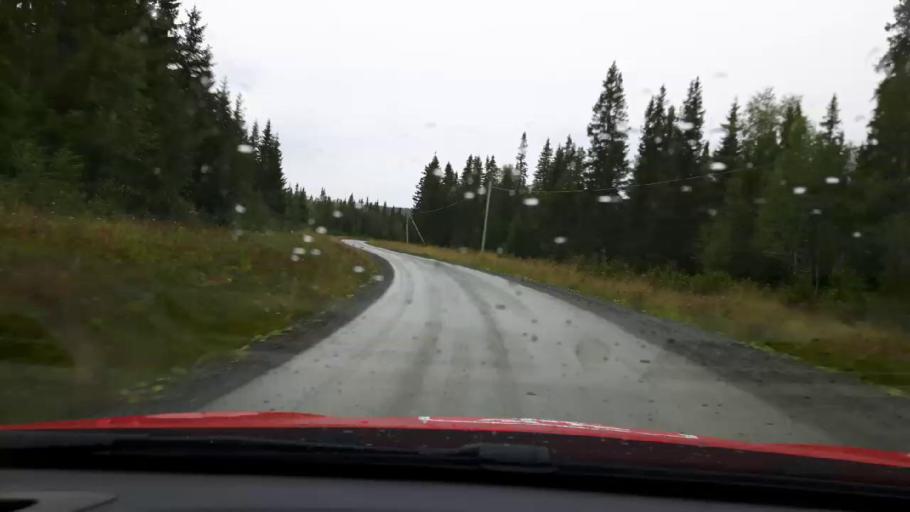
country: SE
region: Jaemtland
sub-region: Are Kommun
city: Are
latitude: 63.4455
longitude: 12.8044
